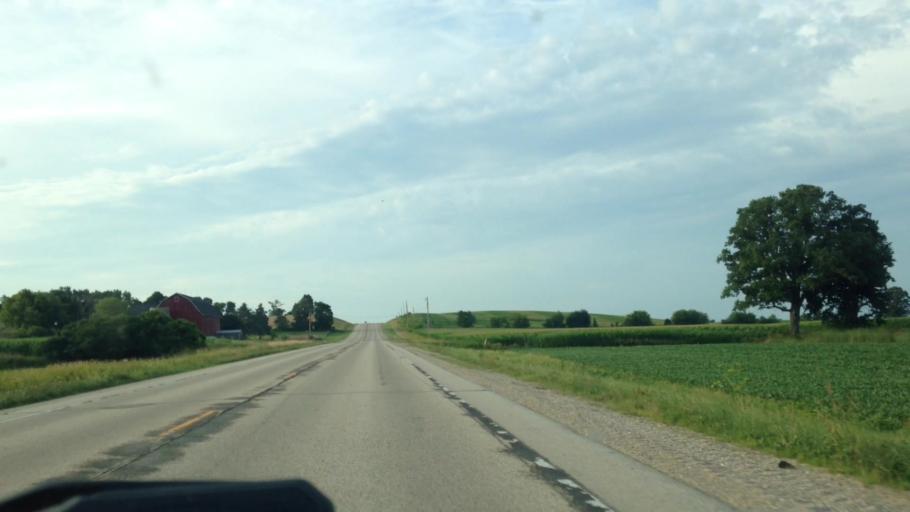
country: US
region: Wisconsin
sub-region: Dodge County
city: Theresa
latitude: 43.4751
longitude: -88.4501
